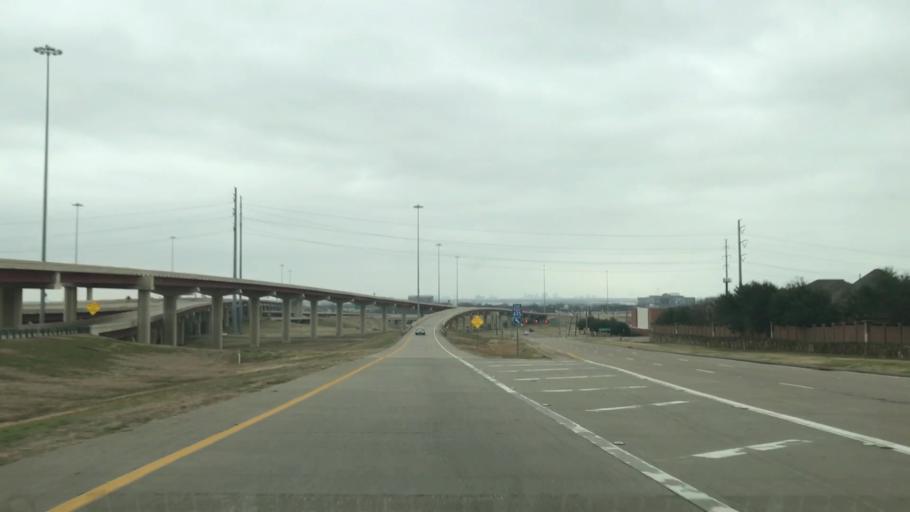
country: US
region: Texas
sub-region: Dallas County
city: Farmers Branch
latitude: 32.9094
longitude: -96.9484
